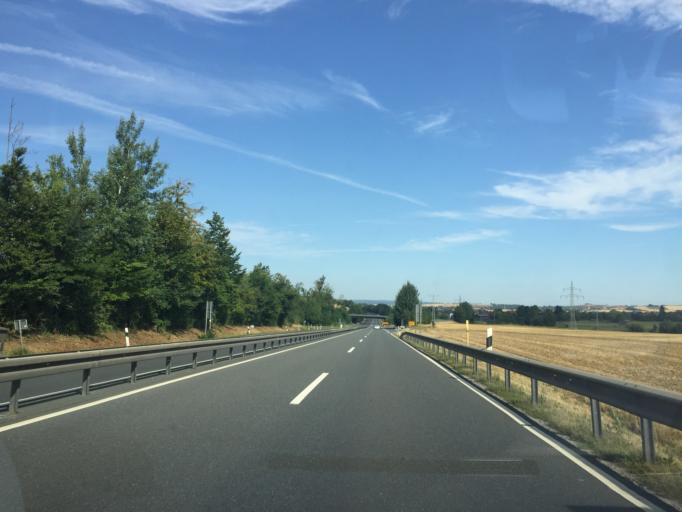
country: DE
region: Lower Saxony
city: Gittelde
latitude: 51.8396
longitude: 10.1811
